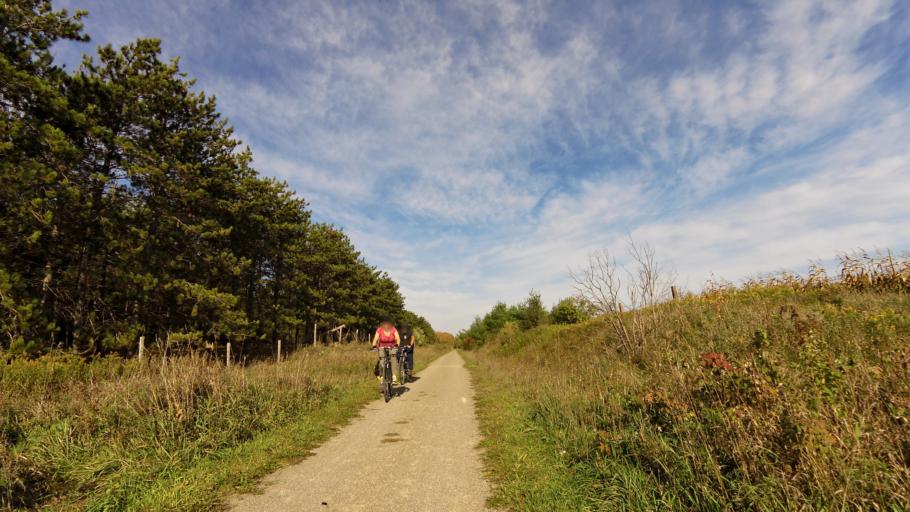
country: CA
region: Ontario
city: Orangeville
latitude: 43.7935
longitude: -80.0468
